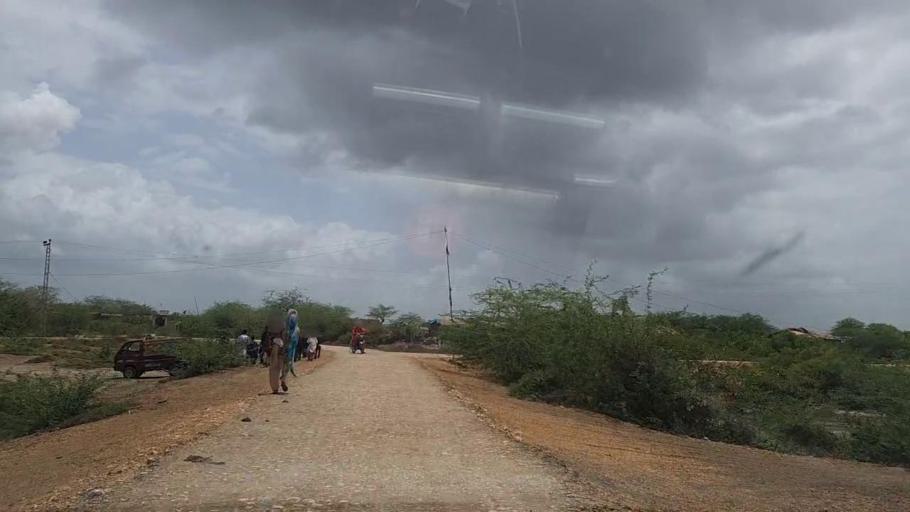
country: PK
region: Sindh
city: Thatta
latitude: 24.6210
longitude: 68.0264
